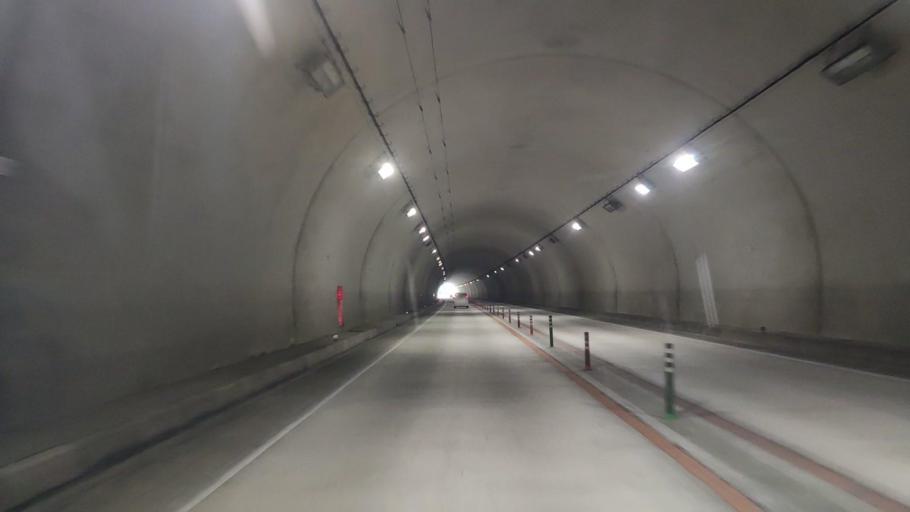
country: JP
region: Wakayama
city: Shingu
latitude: 33.6161
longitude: 135.9172
